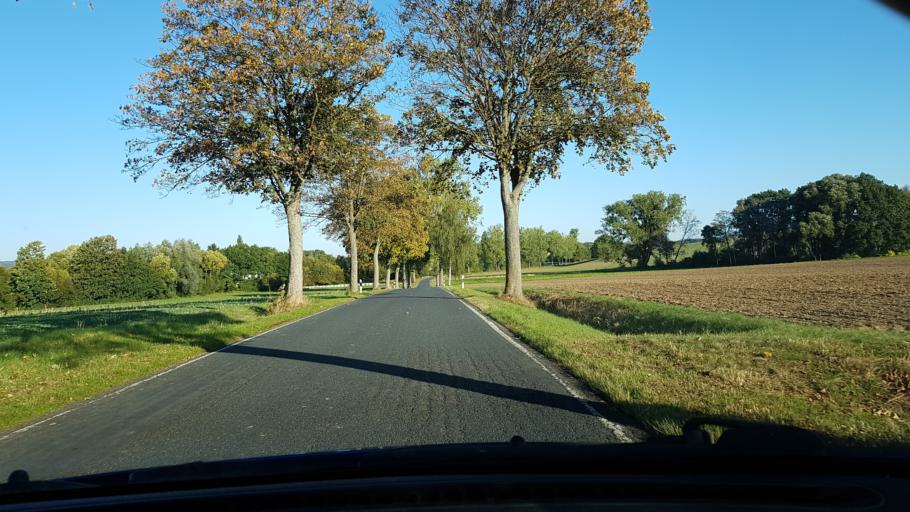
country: DE
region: Lower Saxony
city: Messenkamp
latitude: 52.2139
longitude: 9.4102
